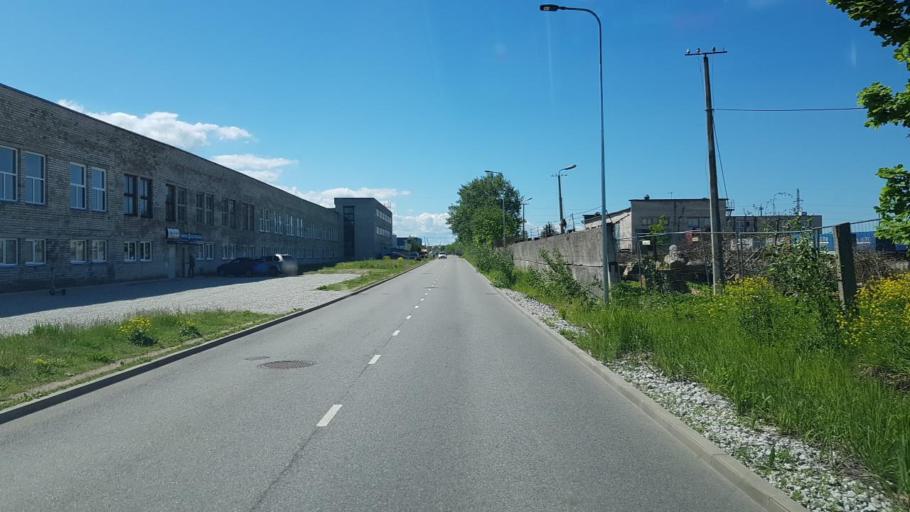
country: EE
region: Ida-Virumaa
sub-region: Narva linn
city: Narva
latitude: 59.3757
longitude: 28.1627
